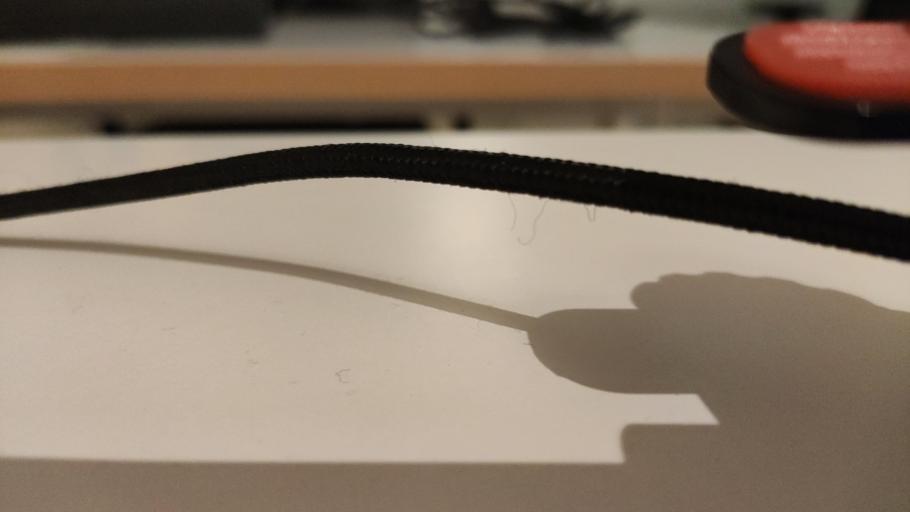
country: RU
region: Moskovskaya
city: Shemetovo
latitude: 56.4114
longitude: 37.9948
